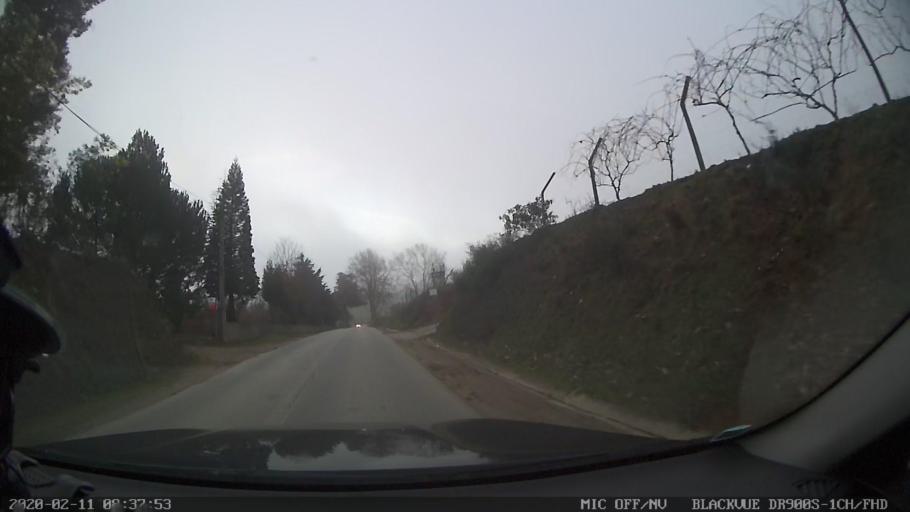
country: PT
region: Vila Real
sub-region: Sabrosa
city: Sabrosa
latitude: 41.2535
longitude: -7.5858
